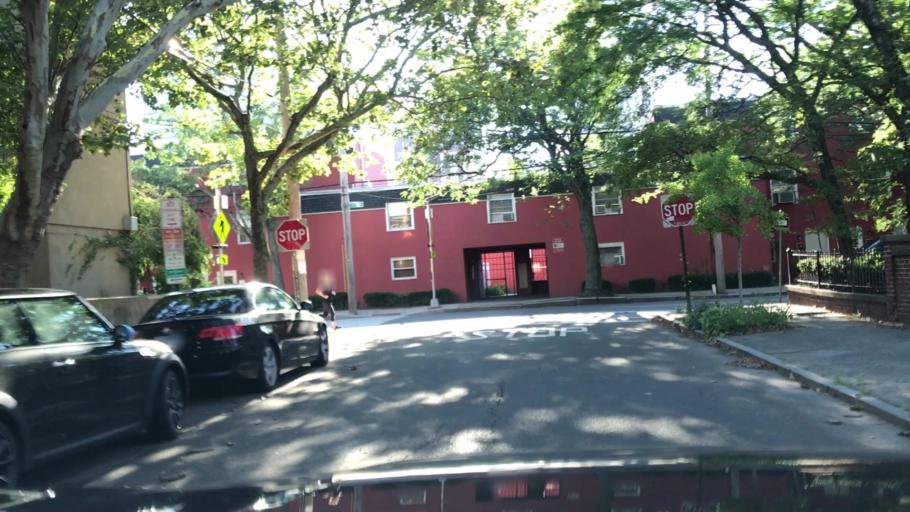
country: US
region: Connecticut
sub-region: New Haven County
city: New Haven
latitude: 41.3058
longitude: -72.9193
